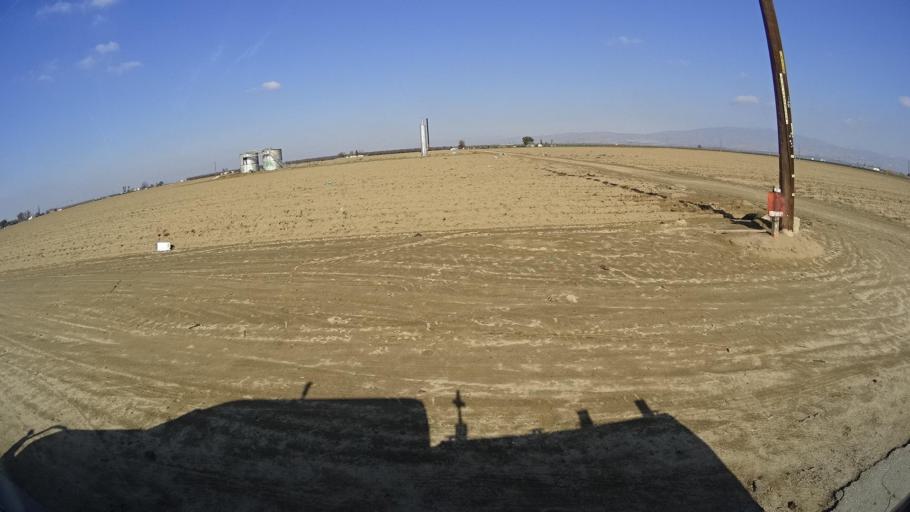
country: US
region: California
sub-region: Kern County
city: Arvin
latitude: 35.2235
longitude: -118.8356
